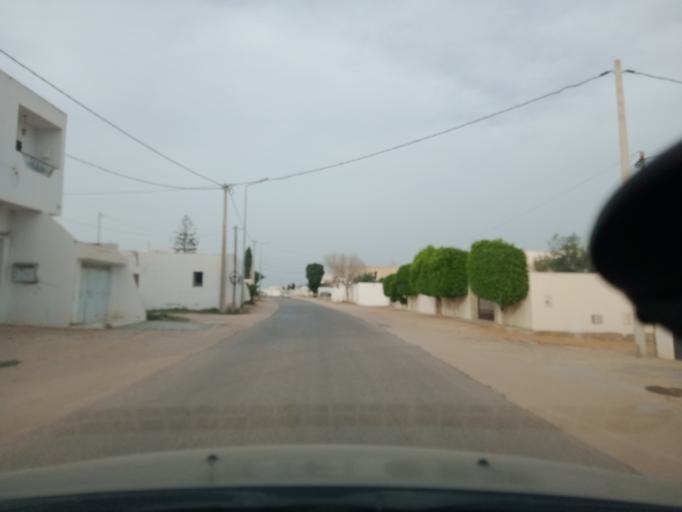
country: TN
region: Safaqis
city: Al Qarmadah
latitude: 34.7858
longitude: 10.7641
